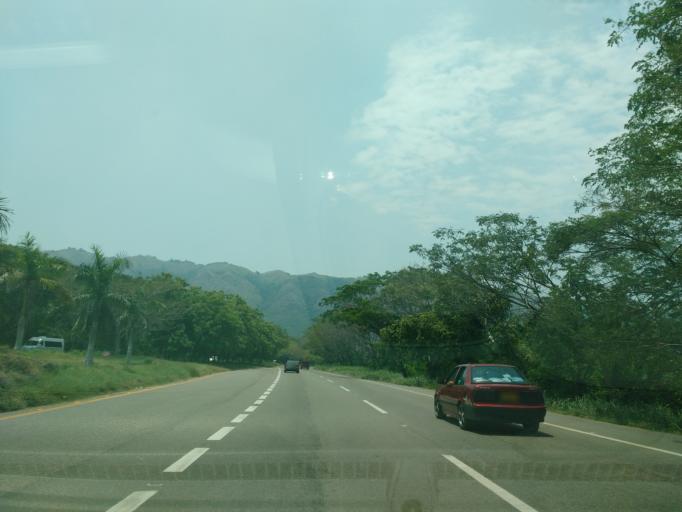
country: CO
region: Cundinamarca
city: Ricaurte
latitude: 4.2410
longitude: -74.7213
